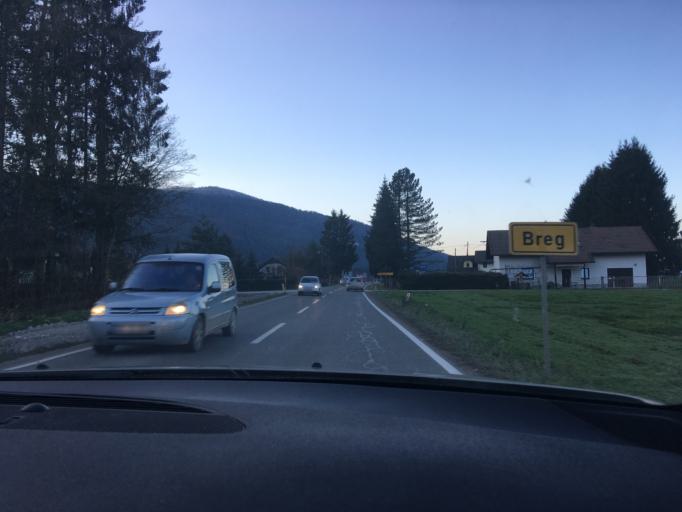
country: SI
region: Kocevje
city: Kocevje
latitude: 45.6566
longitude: 14.8454
